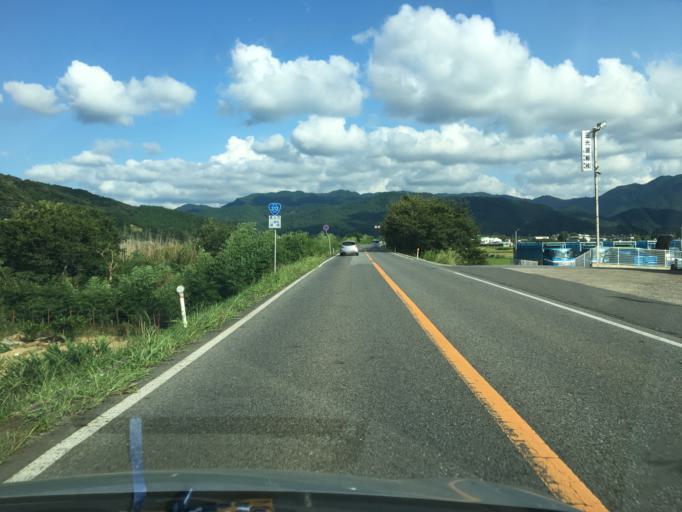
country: JP
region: Hyogo
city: Toyooka
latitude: 35.4418
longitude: 134.7811
